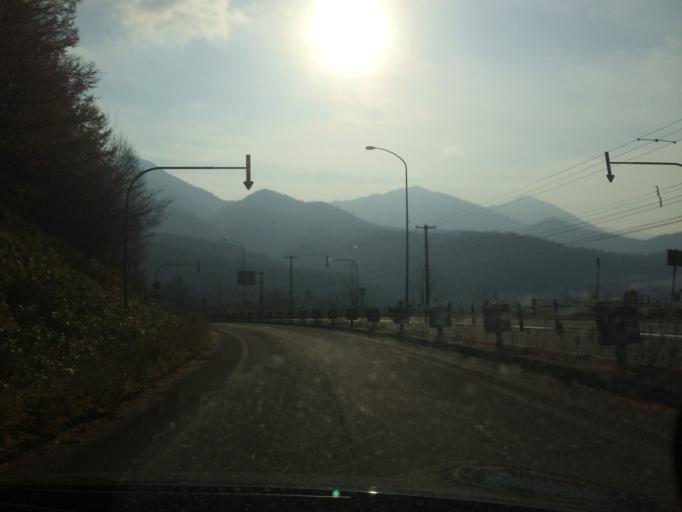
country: JP
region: Hokkaido
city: Shimo-furano
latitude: 42.8839
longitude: 142.2793
